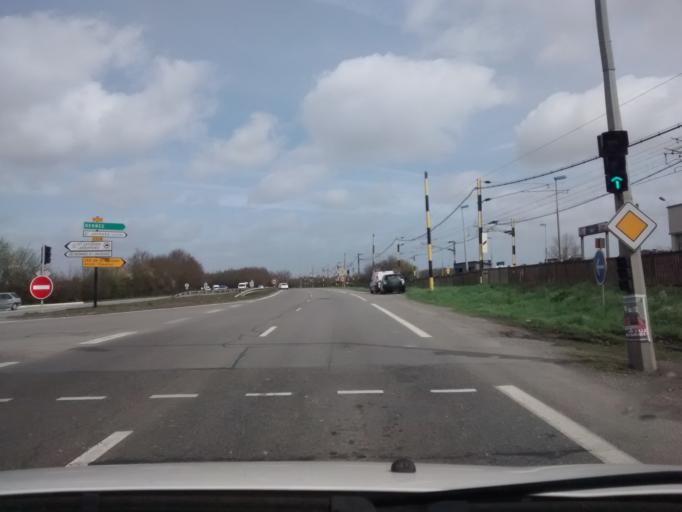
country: FR
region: Brittany
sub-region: Departement d'Ille-et-Vilaine
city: Saint-Jacques-de-la-Lande
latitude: 48.0673
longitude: -1.7143
